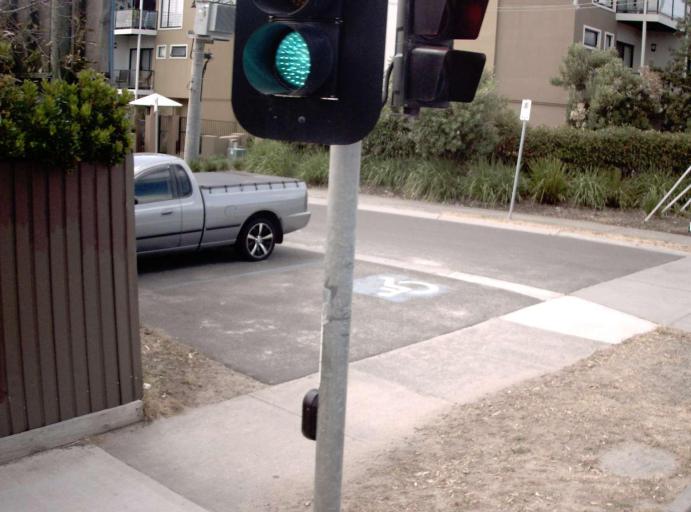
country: AU
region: Victoria
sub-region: Frankston
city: Frankston East
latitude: -38.1208
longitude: 145.1250
